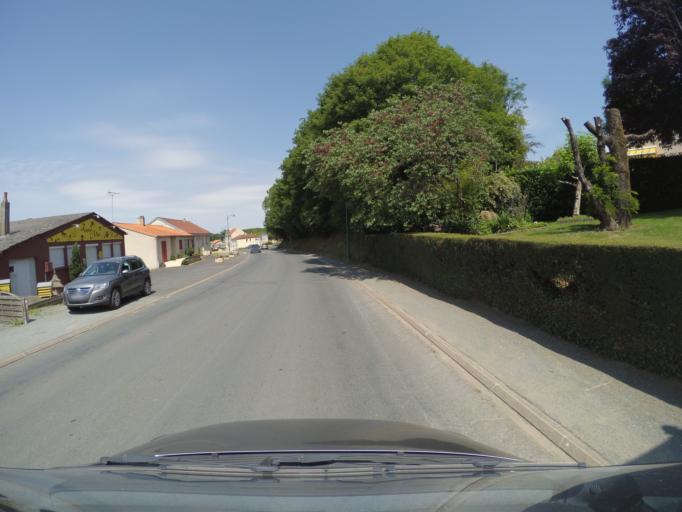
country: FR
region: Pays de la Loire
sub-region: Departement de la Vendee
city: Saint-Michel-Mont-Mercure
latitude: 46.8320
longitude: -0.8852
